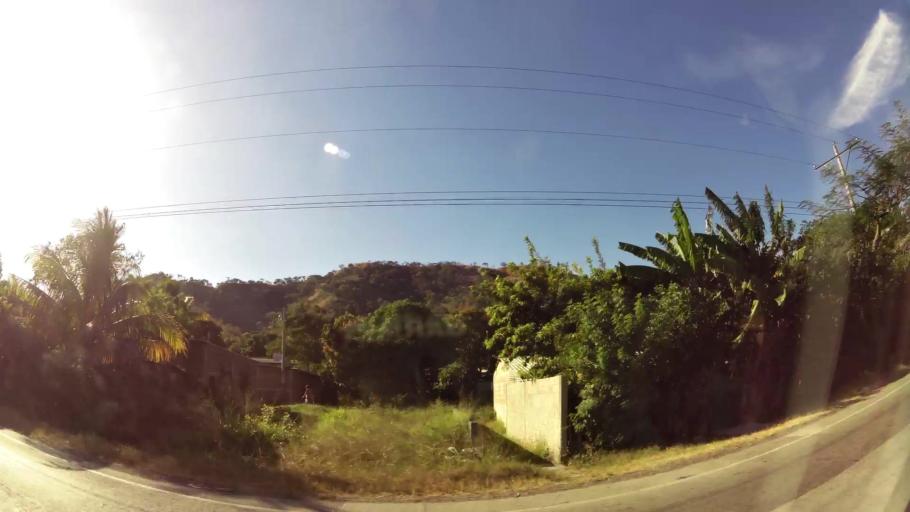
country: SV
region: Santa Ana
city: Santa Ana
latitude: 14.0367
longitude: -89.5223
